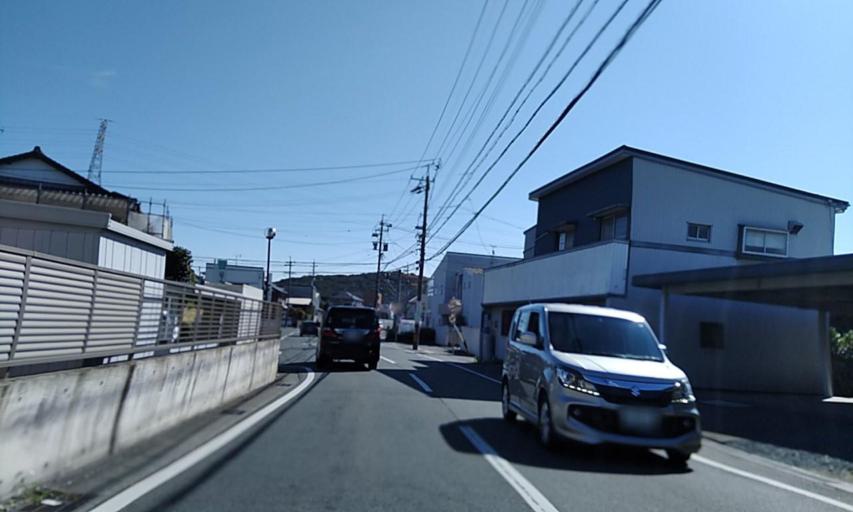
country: JP
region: Aichi
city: Toyohashi
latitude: 34.7402
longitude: 137.4227
